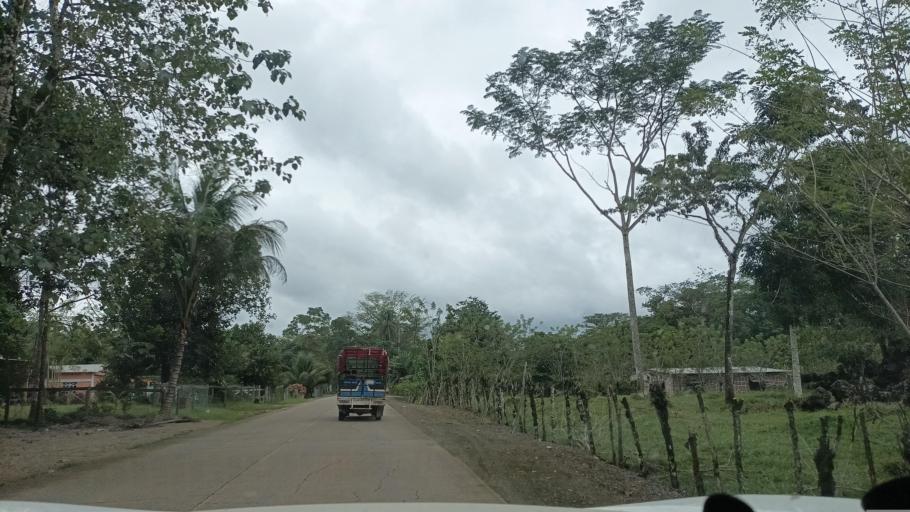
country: MX
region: Veracruz
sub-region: Uxpanapa
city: Poblado 10
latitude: 17.2789
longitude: -94.4824
